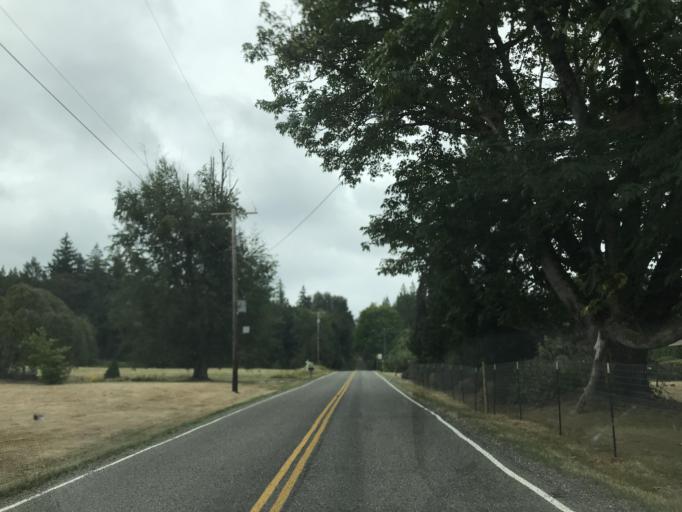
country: US
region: Washington
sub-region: Whatcom County
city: Sudden Valley
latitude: 48.7895
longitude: -122.3330
